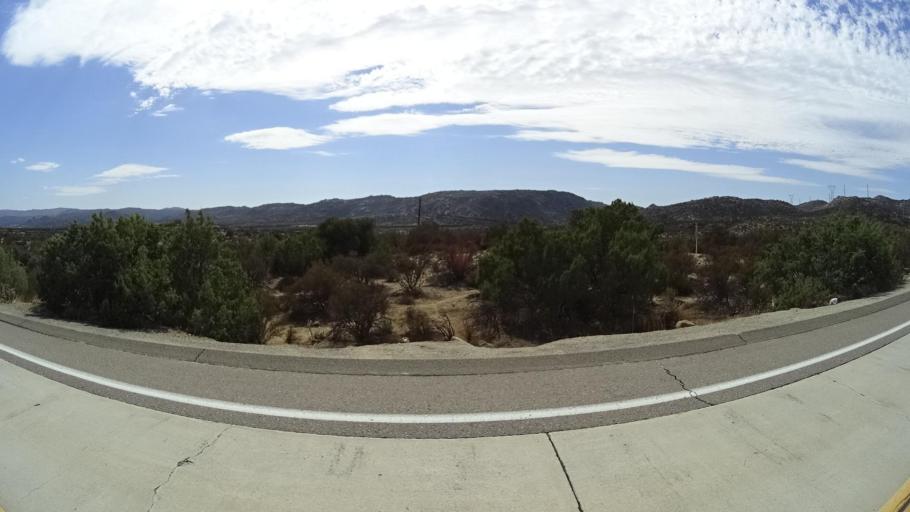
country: MX
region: Baja California
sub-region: Tecate
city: Cereso del Hongo
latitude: 32.6165
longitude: -116.2134
